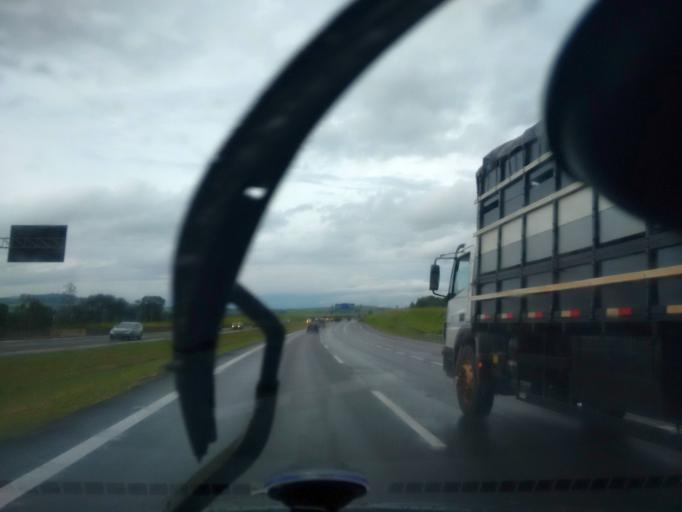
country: BR
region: Sao Paulo
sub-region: Limeira
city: Limeira
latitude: -22.5776
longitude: -47.4593
